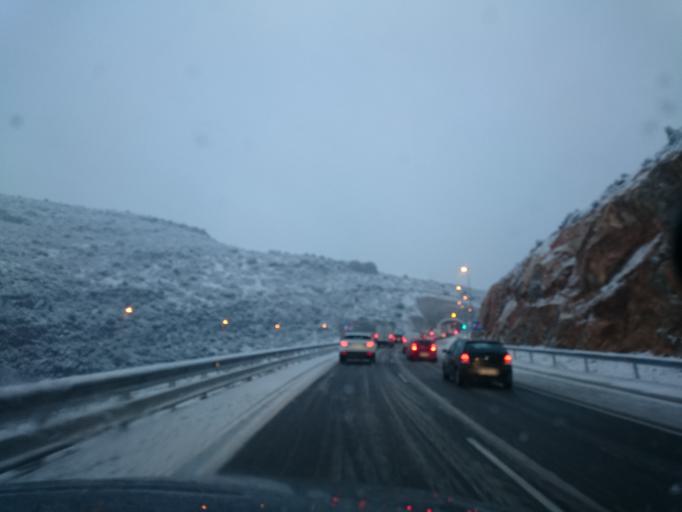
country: ES
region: Catalonia
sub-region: Provincia de Barcelona
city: Vilafranca del Penedes
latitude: 41.3055
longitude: 1.7217
